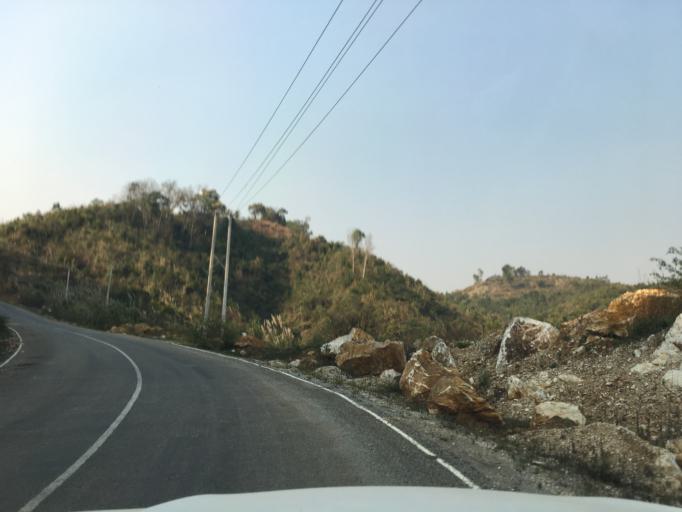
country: LA
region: Houaphan
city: Xam Nua
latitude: 20.5678
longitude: 104.0613
